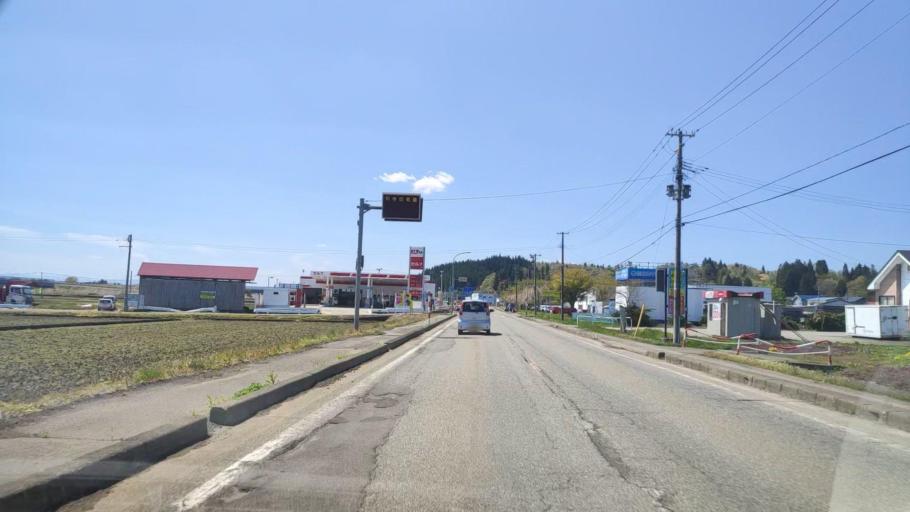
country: JP
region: Akita
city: Omagari
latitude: 39.4357
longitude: 140.4467
